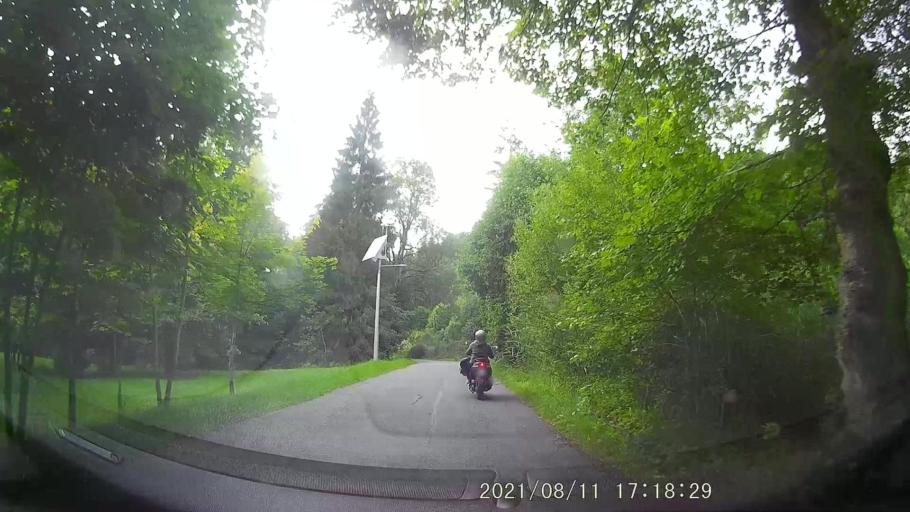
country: PL
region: Lower Silesian Voivodeship
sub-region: Powiat klodzki
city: Polanica-Zdroj
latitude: 50.3038
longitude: 16.5270
